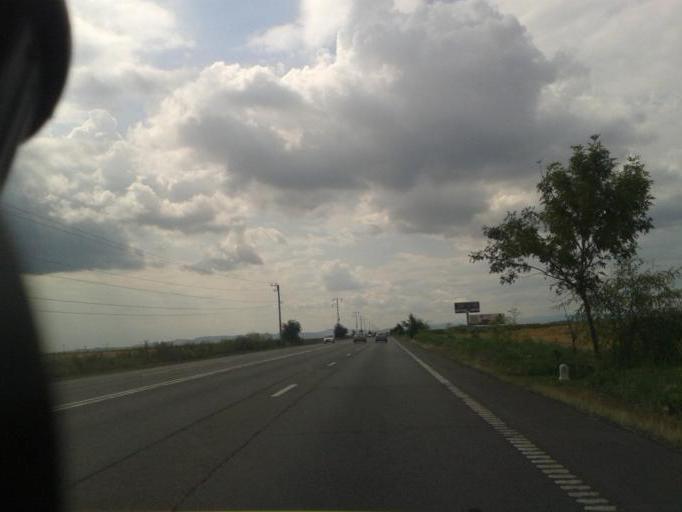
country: RO
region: Prahova
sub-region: Oras Baicoi
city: Tintea
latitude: 44.9903
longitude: 25.9126
